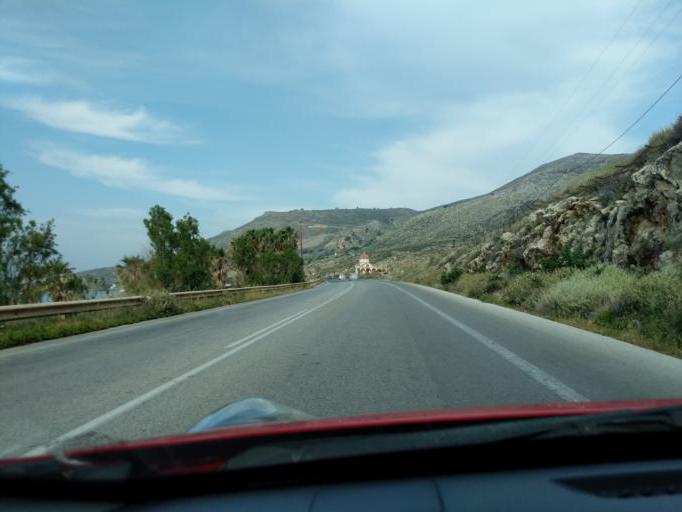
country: GR
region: Crete
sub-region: Nomos Rethymnis
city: Atsipopoulon
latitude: 35.3506
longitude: 24.3551
